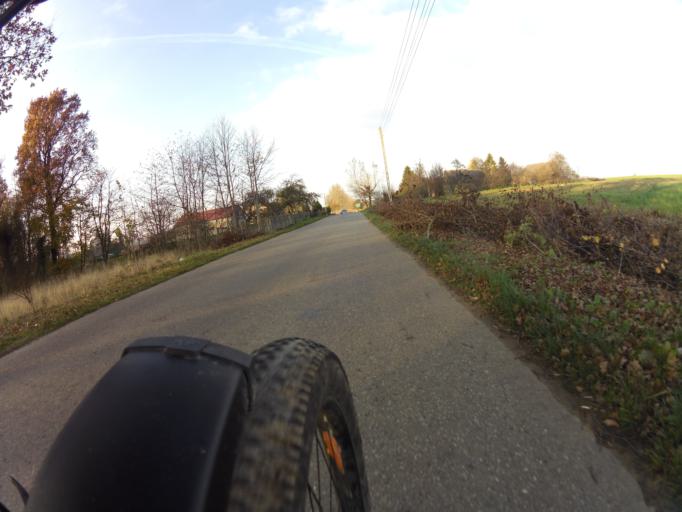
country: PL
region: Pomeranian Voivodeship
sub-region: Powiat pucki
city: Krokowa
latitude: 54.7673
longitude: 18.1801
